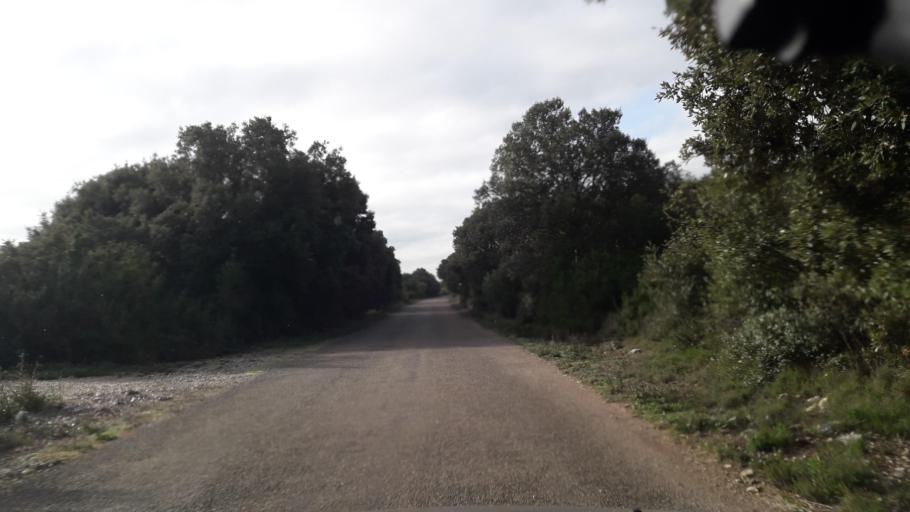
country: FR
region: Languedoc-Roussillon
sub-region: Departement du Gard
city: Saint-Julien-de-Peyrolas
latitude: 44.3471
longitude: 4.5270
